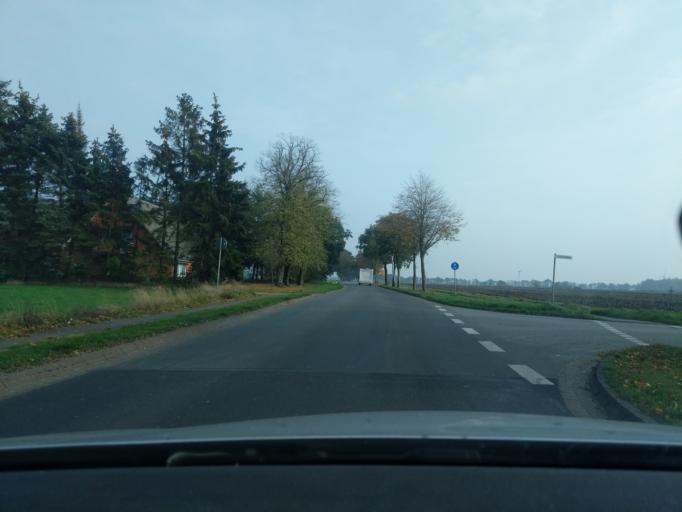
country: DE
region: Lower Saxony
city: Mittelstenahe
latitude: 53.6497
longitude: 9.0441
